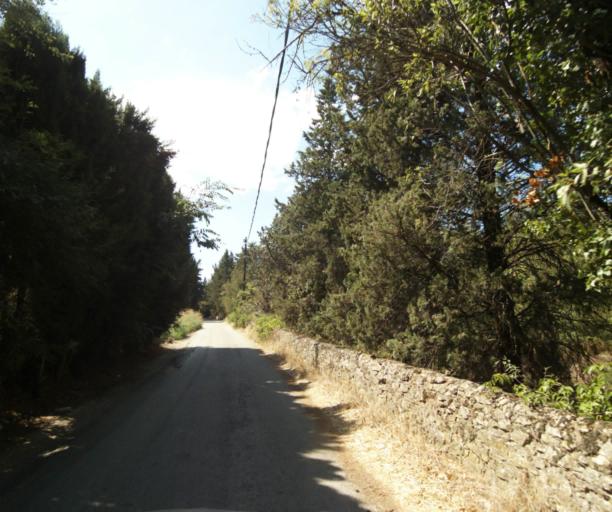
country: FR
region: Languedoc-Roussillon
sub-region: Departement du Gard
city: Rodilhan
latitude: 43.8228
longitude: 4.4141
